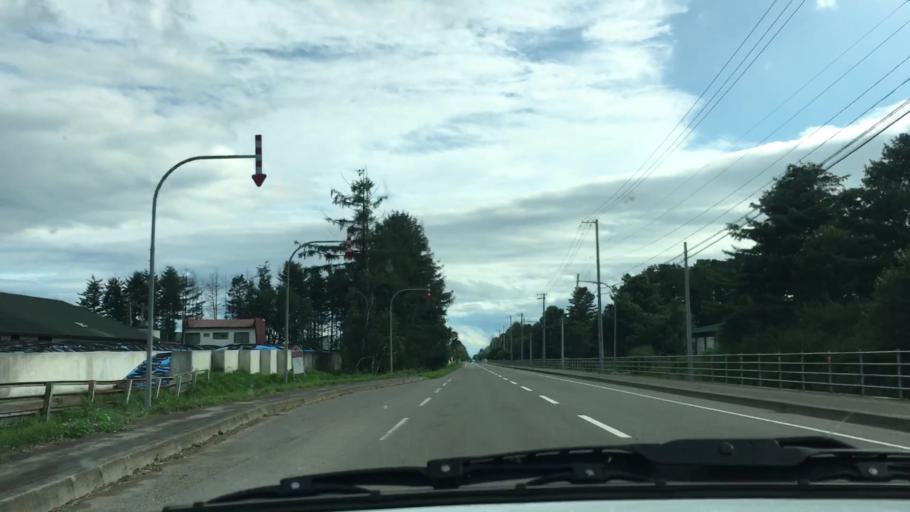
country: JP
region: Hokkaido
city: Otofuke
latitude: 43.2493
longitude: 143.2989
